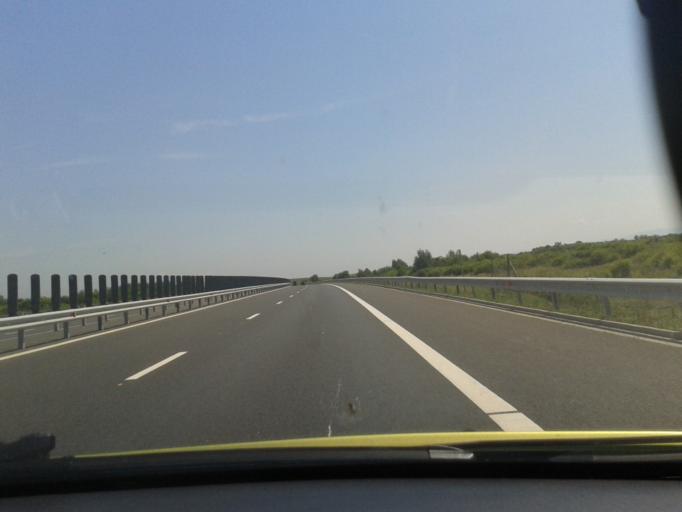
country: RO
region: Timis
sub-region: Comuna Bethausen
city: Bethausen
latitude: 45.8103
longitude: 21.9406
